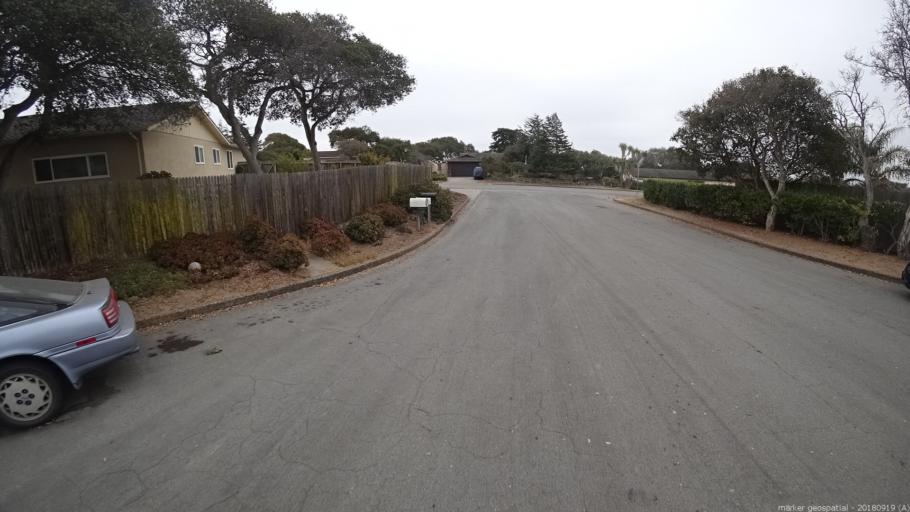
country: US
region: California
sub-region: Monterey County
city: Prunedale
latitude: 36.7795
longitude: -121.7100
